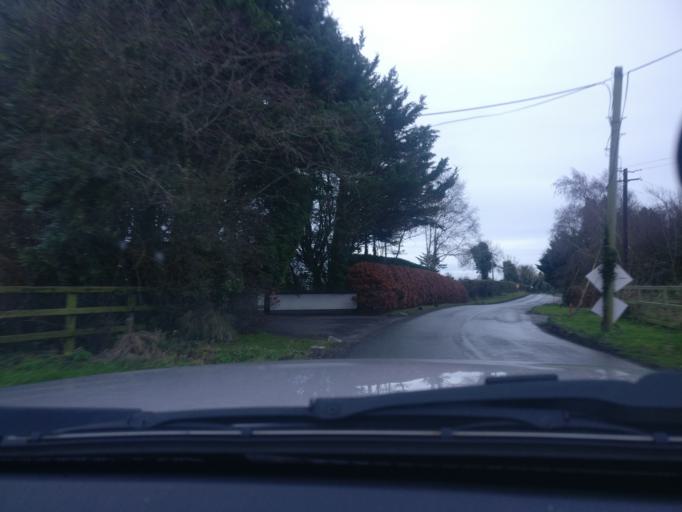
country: IE
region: Leinster
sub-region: Kildare
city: Maynooth
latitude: 53.4499
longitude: -6.6195
